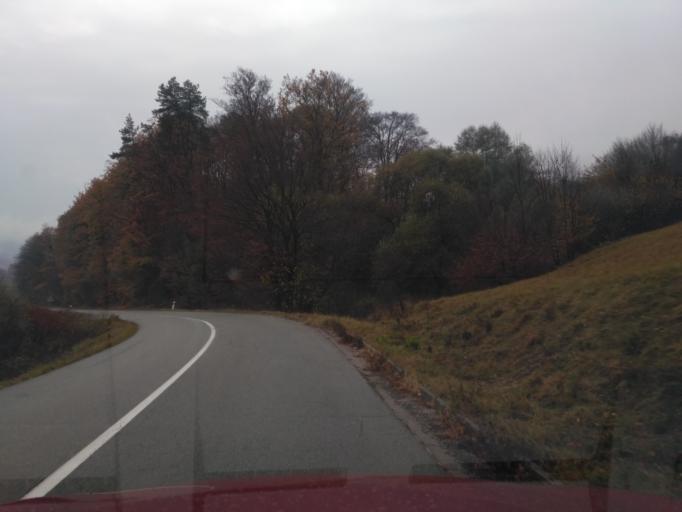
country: SK
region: Kosicky
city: Medzev
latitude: 48.7081
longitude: 20.8036
